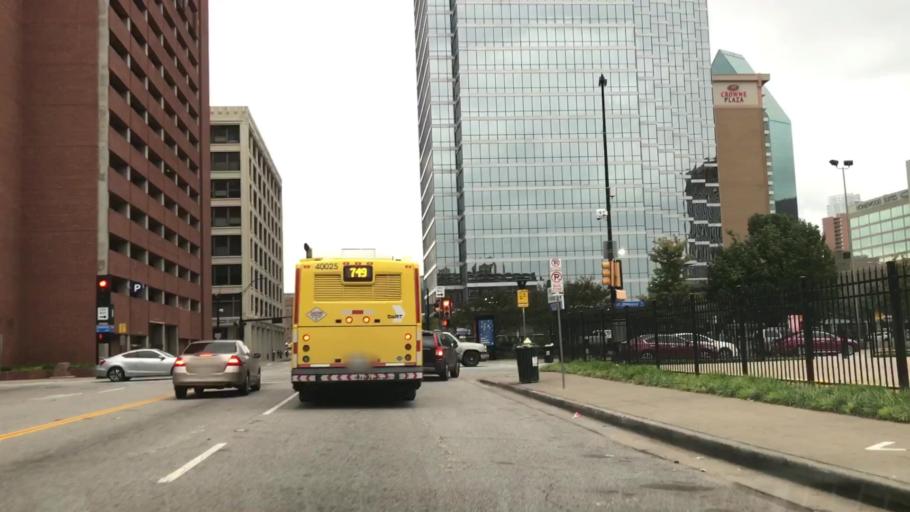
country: US
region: Texas
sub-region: Dallas County
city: Dallas
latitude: 32.7785
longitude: -96.8039
